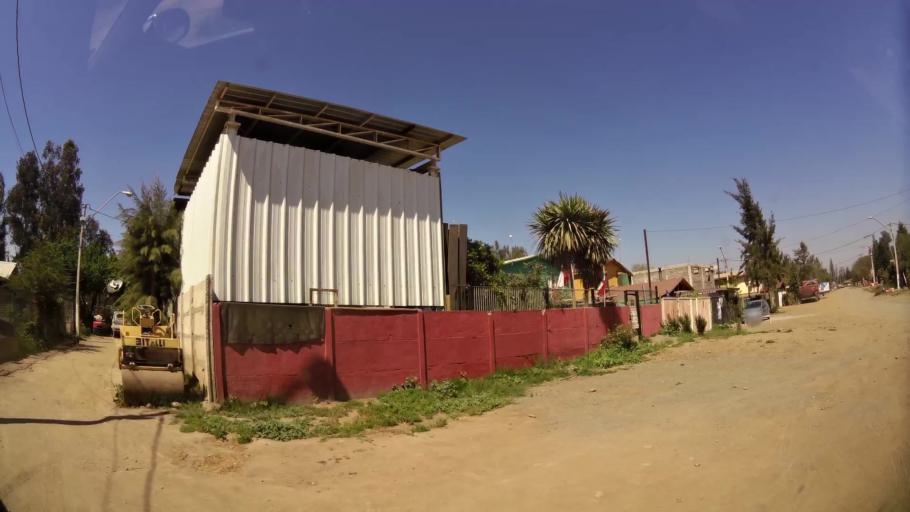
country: CL
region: Santiago Metropolitan
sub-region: Provincia de Talagante
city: Penaflor
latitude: -33.5848
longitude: -70.8054
